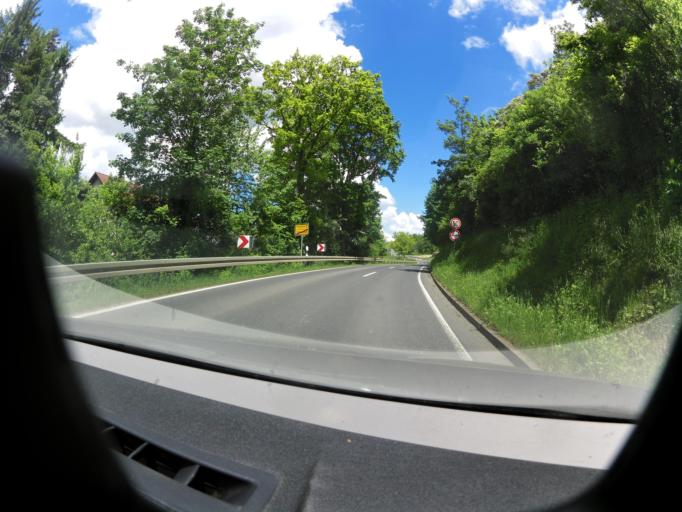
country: DE
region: Bavaria
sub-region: Regierungsbezirk Unterfranken
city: Schwanfeld
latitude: 49.9255
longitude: 10.1369
